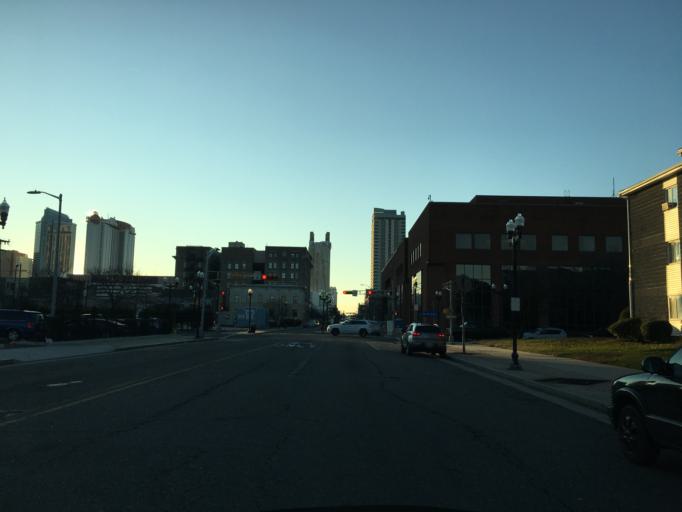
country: US
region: New Jersey
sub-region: Atlantic County
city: Atlantic City
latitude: 39.3652
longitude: -74.4269
